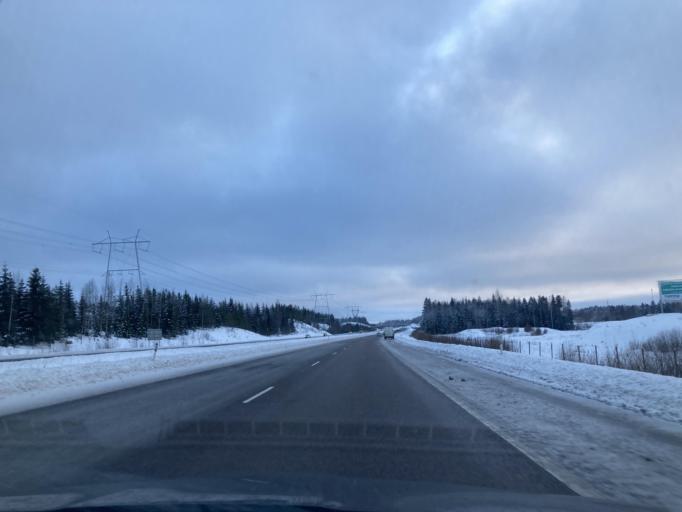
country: FI
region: Uusimaa
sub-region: Porvoo
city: Pukkila
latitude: 60.8075
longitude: 25.5065
